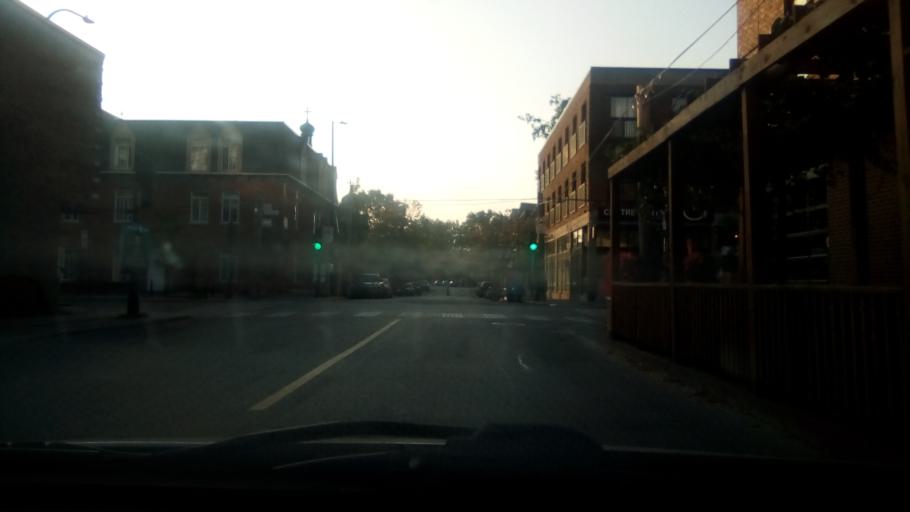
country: CA
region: Quebec
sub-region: Montreal
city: Montreal
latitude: 45.4832
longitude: -73.5624
